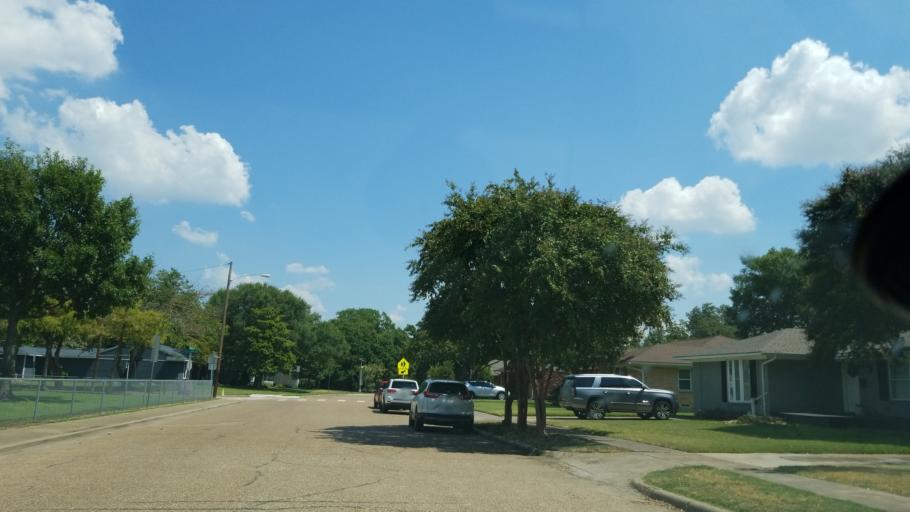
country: US
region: Texas
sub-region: Dallas County
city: Richardson
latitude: 32.8830
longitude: -96.7078
